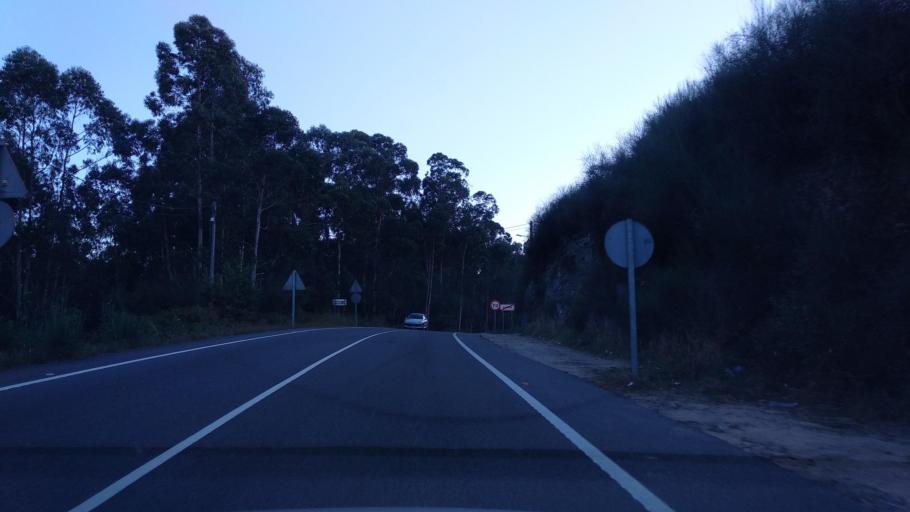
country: ES
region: Galicia
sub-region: Provincia de Pontevedra
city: Marin
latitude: 42.3453
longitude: -8.6441
